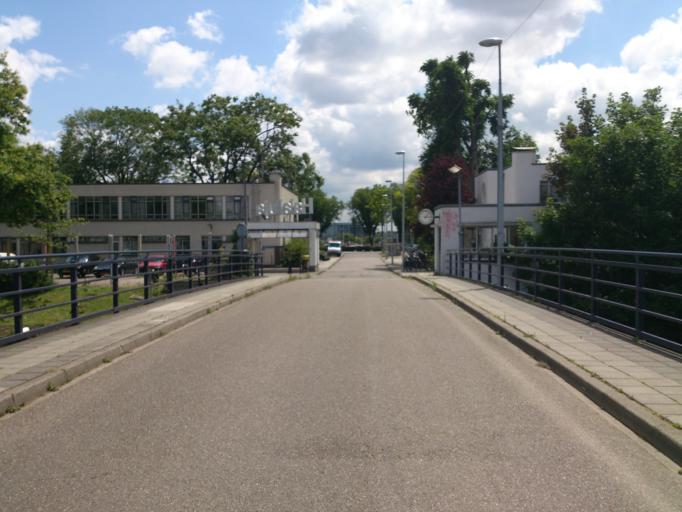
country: NL
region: North Holland
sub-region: Gemeente Amsterdam
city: Amsterdam
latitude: 52.3844
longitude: 4.9050
